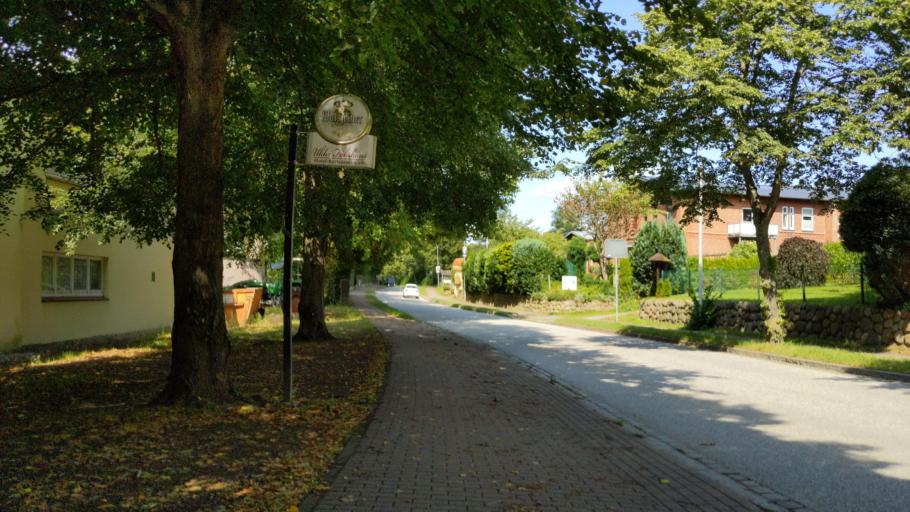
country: DE
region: Schleswig-Holstein
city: Eutin
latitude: 54.1800
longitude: 10.6233
